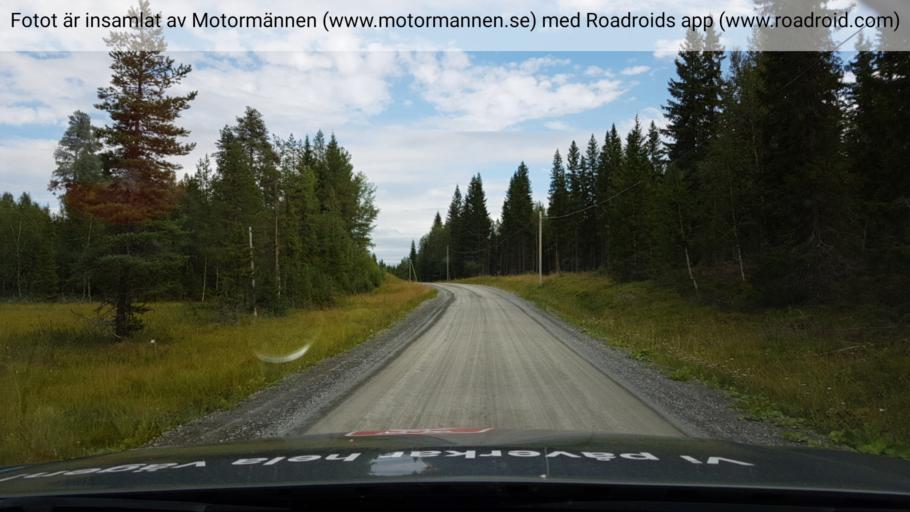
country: SE
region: Jaemtland
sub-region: Krokoms Kommun
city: Valla
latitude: 63.7116
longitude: 13.5384
